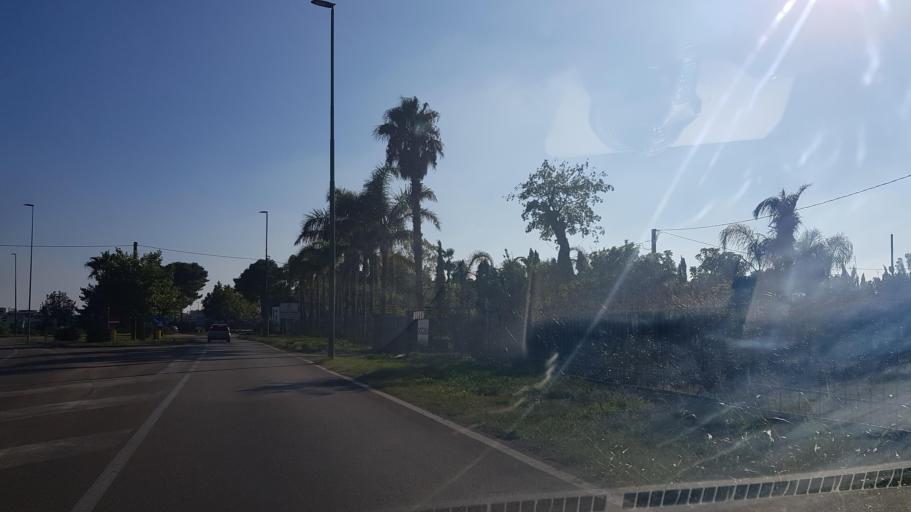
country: IT
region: Apulia
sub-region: Provincia di Lecce
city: Montesano Salentino
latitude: 39.9837
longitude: 18.3228
